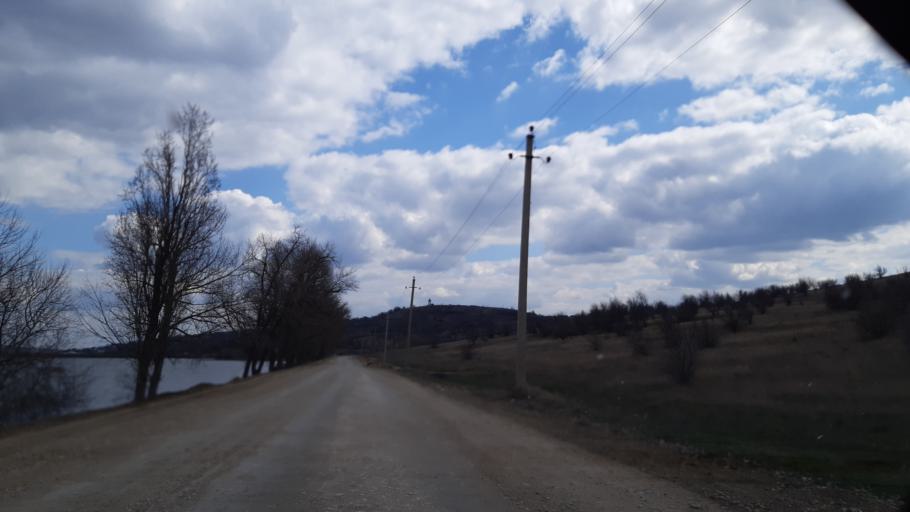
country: MD
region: Laloveni
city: Ialoveni
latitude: 46.8825
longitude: 28.7388
